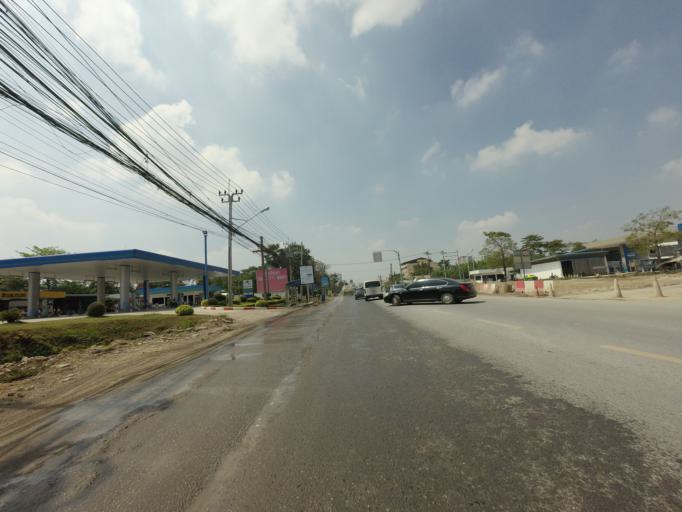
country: TH
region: Bangkok
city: Suan Luang
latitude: 13.7477
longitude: 100.6565
